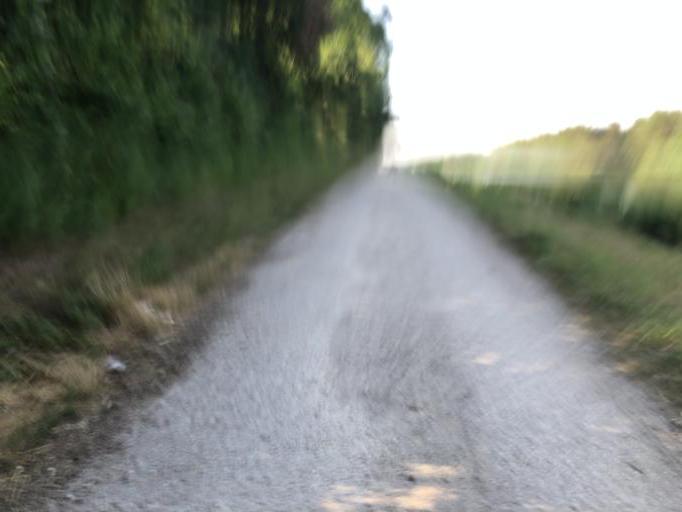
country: DE
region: Bavaria
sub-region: Regierungsbezirk Mittelfranken
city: Erlangen
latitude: 49.5945
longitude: 10.9714
